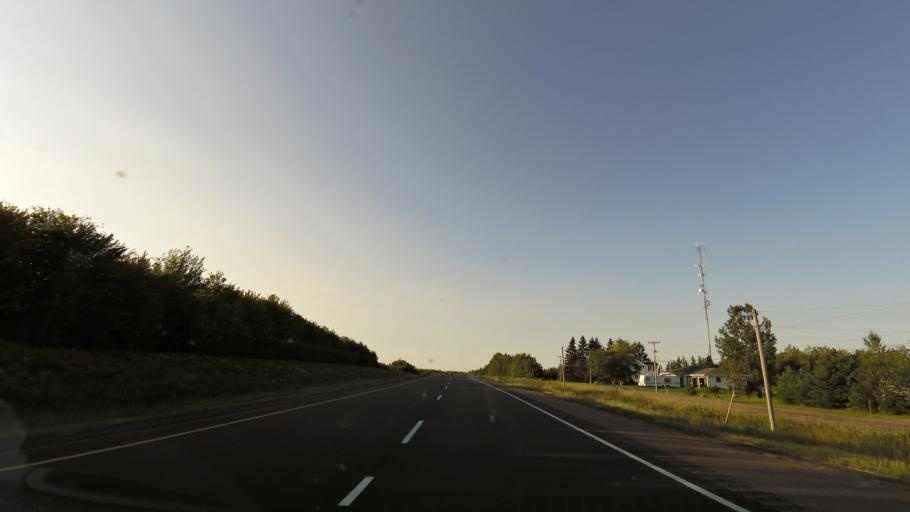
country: CA
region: New Brunswick
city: Dieppe
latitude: 46.0838
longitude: -64.5941
